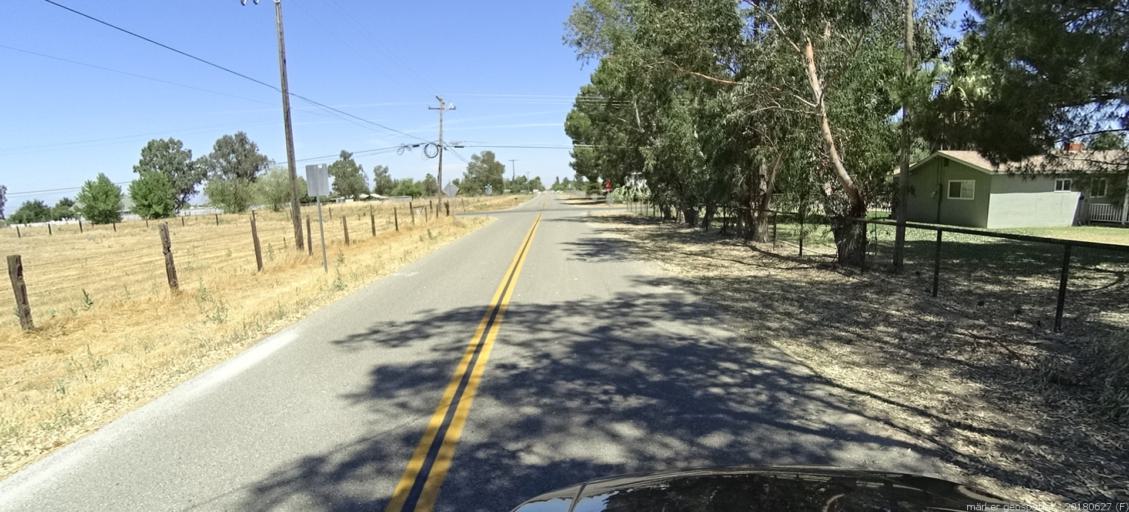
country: US
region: California
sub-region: Madera County
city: Bonadelle Ranchos-Madera Ranchos
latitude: 36.9521
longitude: -119.9127
